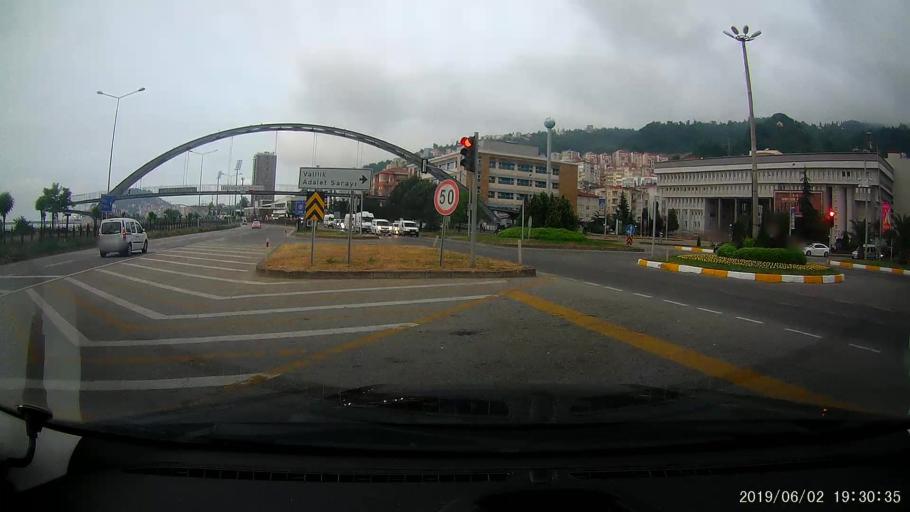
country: TR
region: Giresun
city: Giresun
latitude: 40.9086
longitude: 38.3656
